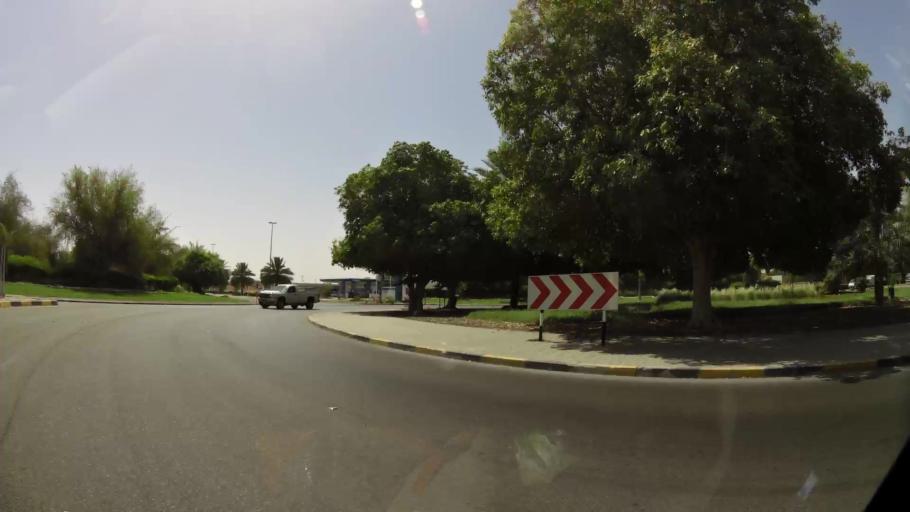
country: OM
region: Al Buraimi
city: Al Buraymi
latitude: 24.2873
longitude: 55.7674
